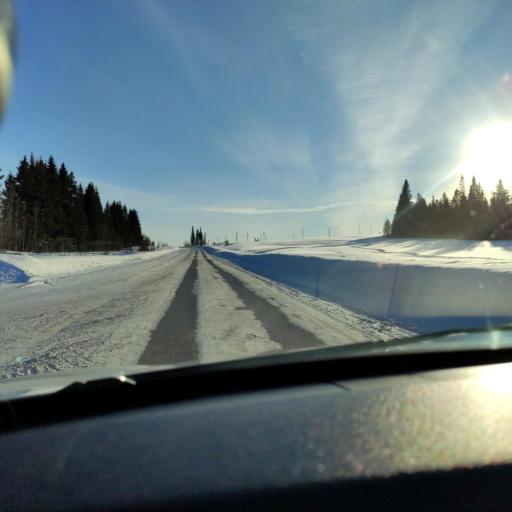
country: RU
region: Perm
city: Polazna
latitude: 58.3395
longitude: 56.4378
